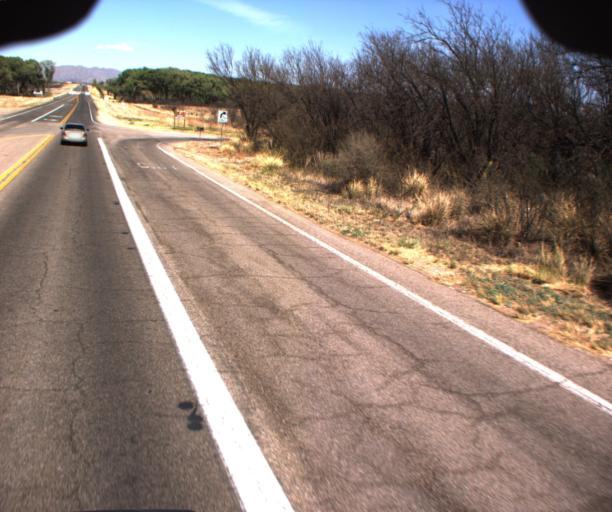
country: US
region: Arizona
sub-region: Cochise County
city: Sierra Vista Southeast
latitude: 31.5503
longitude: -110.1433
